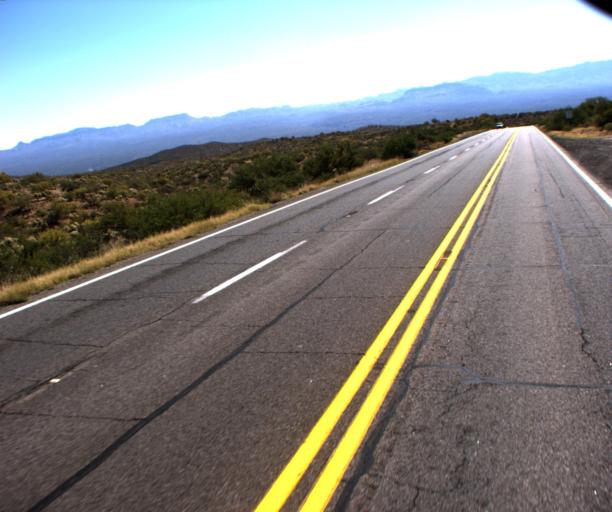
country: US
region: Arizona
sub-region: Pinal County
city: Mammoth
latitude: 32.6600
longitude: -110.6934
